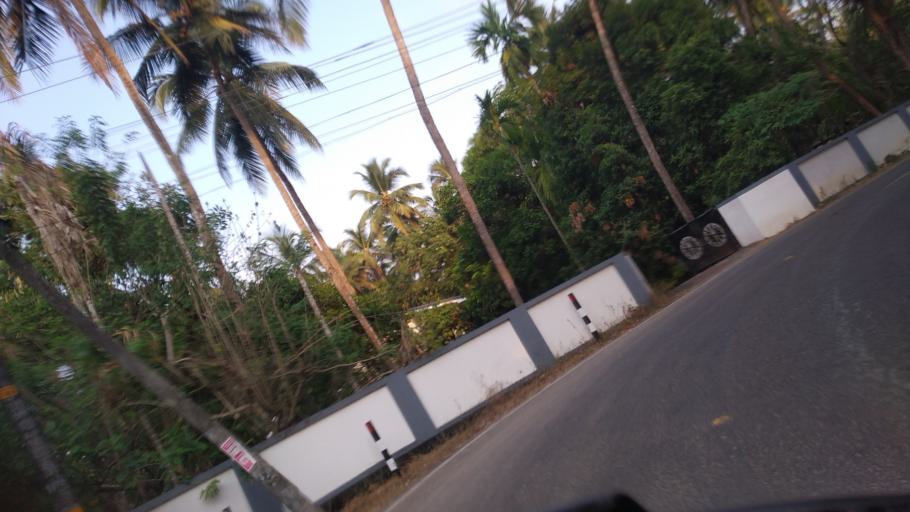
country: IN
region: Kerala
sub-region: Thrissur District
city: Thanniyam
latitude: 10.3775
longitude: 76.1022
